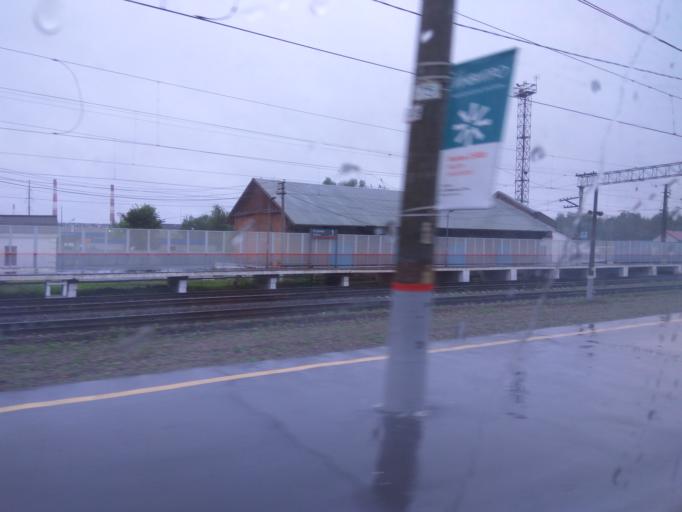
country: RU
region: Moskovskaya
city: Stupino
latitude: 54.9094
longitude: 38.0785
